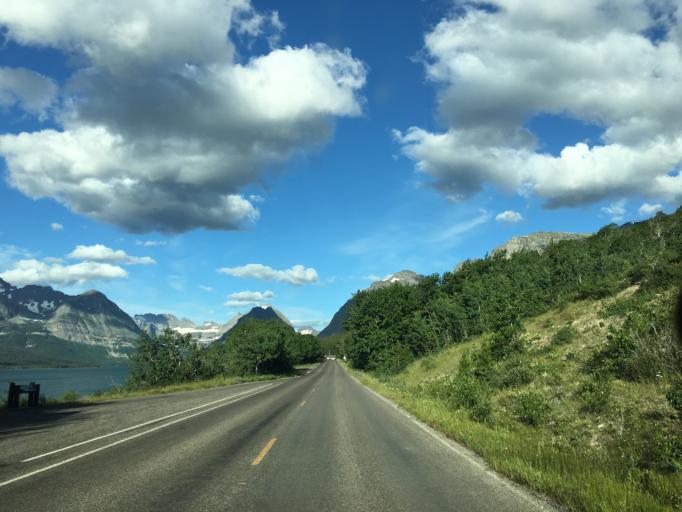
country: CA
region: Alberta
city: Cardston
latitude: 48.8239
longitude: -113.5721
